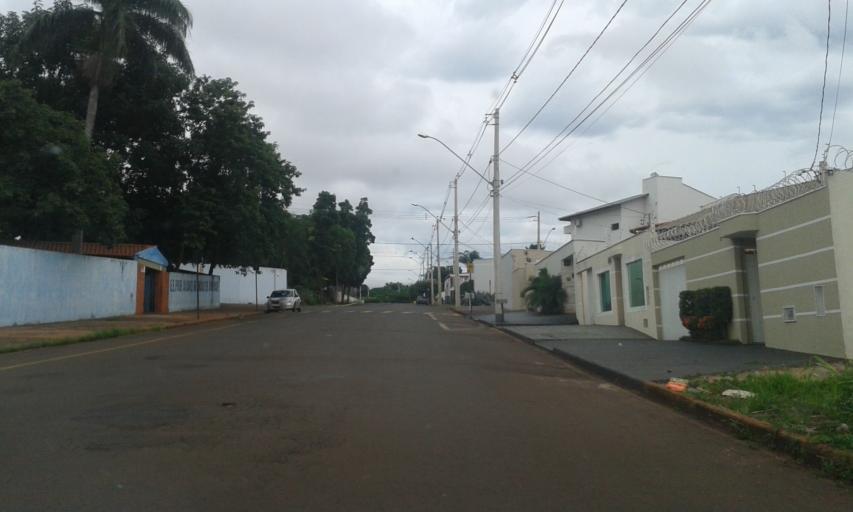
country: BR
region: Minas Gerais
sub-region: Ituiutaba
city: Ituiutaba
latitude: -18.9743
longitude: -49.4510
